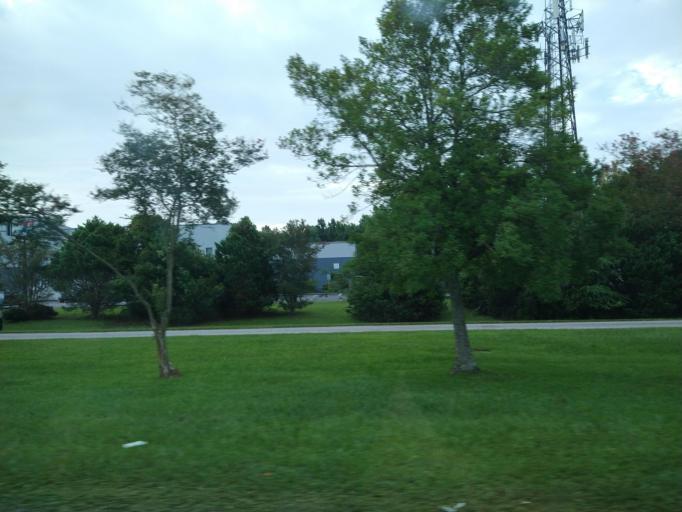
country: US
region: North Carolina
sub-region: Onslow County
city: Jacksonville
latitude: 34.7574
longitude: -77.4202
